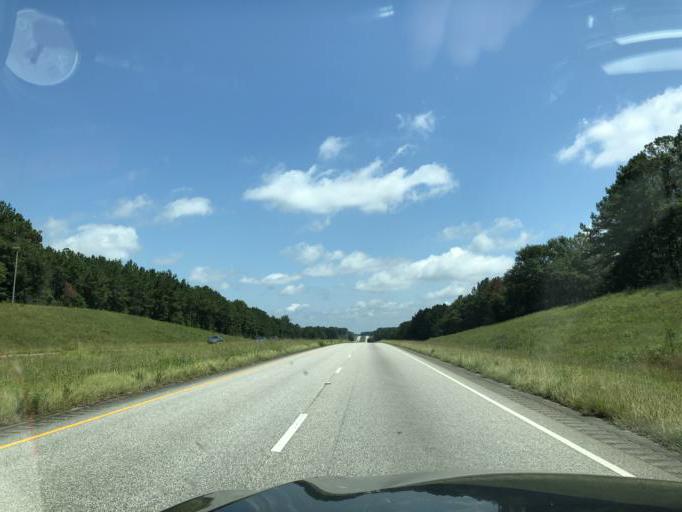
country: US
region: Alabama
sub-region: Barbour County
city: Eufaula
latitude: 31.7473
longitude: -85.2337
